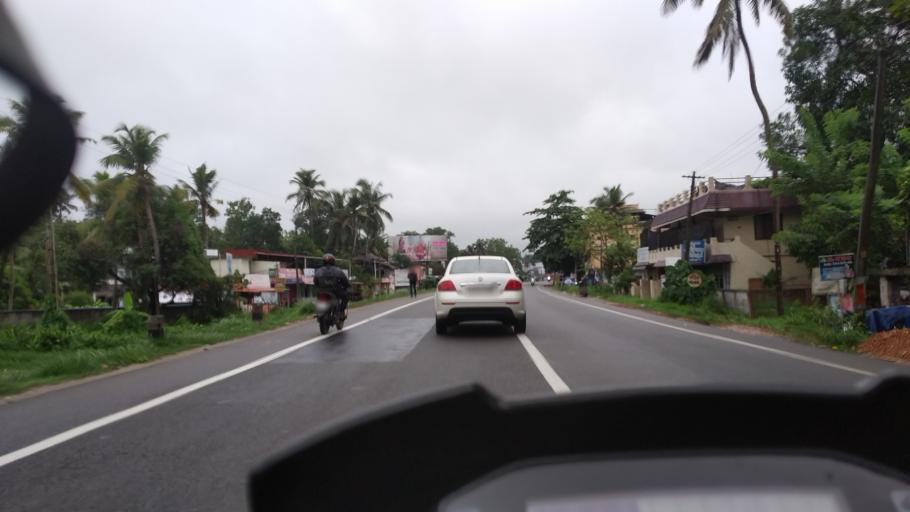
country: IN
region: Kerala
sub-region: Alappuzha
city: Mavelikara
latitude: 9.2725
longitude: 76.4600
